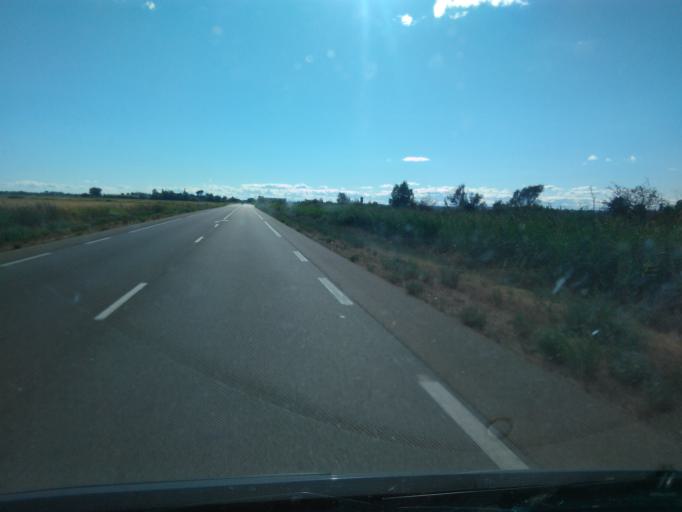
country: FR
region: Languedoc-Roussillon
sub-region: Departement du Gard
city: Bellegarde
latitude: 43.6813
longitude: 4.5227
